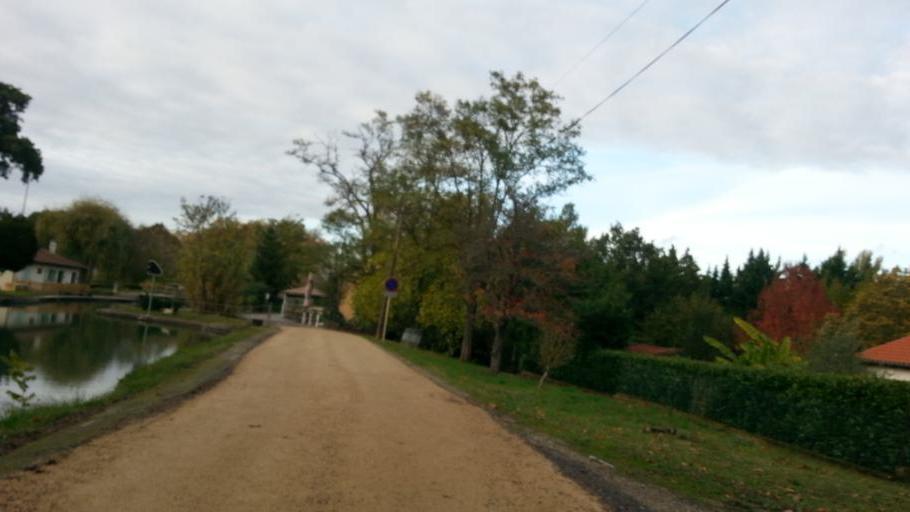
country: FR
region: Midi-Pyrenees
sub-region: Departement de la Haute-Garonne
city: Labege
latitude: 43.5229
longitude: 1.5192
